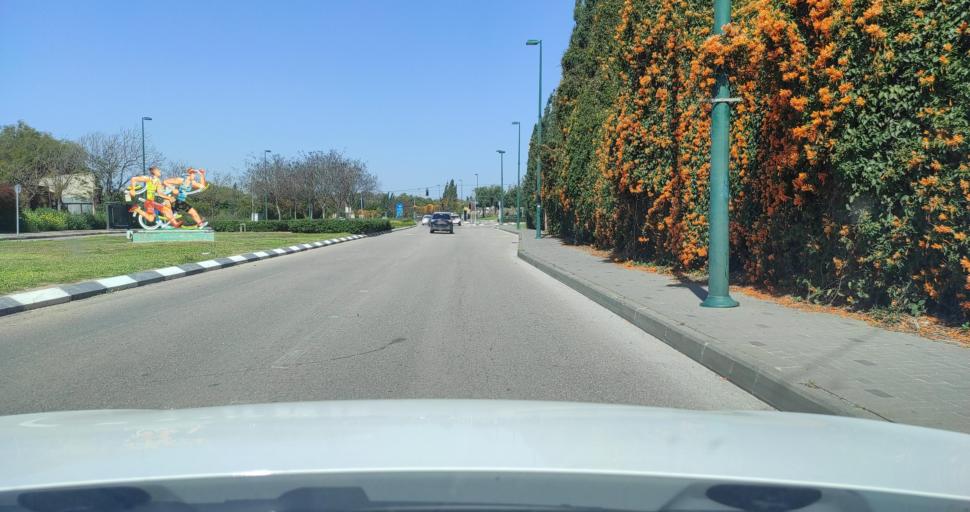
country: IL
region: Central District
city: Bet Yizhaq
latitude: 32.3165
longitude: 34.8809
